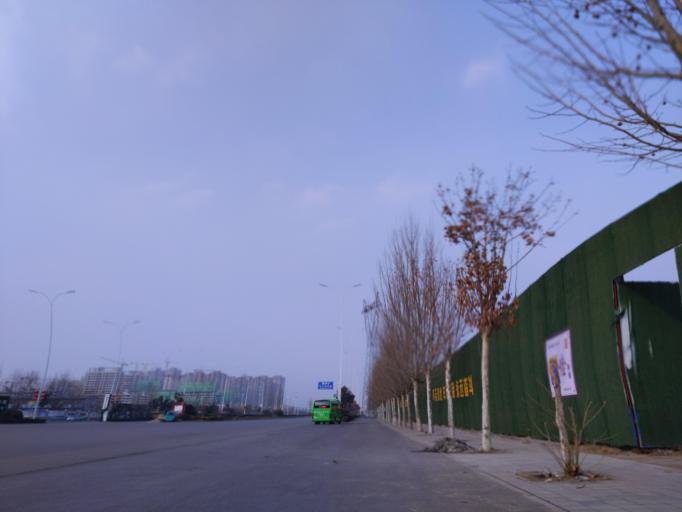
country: CN
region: Henan Sheng
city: Puyang
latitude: 35.8062
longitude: 115.0222
